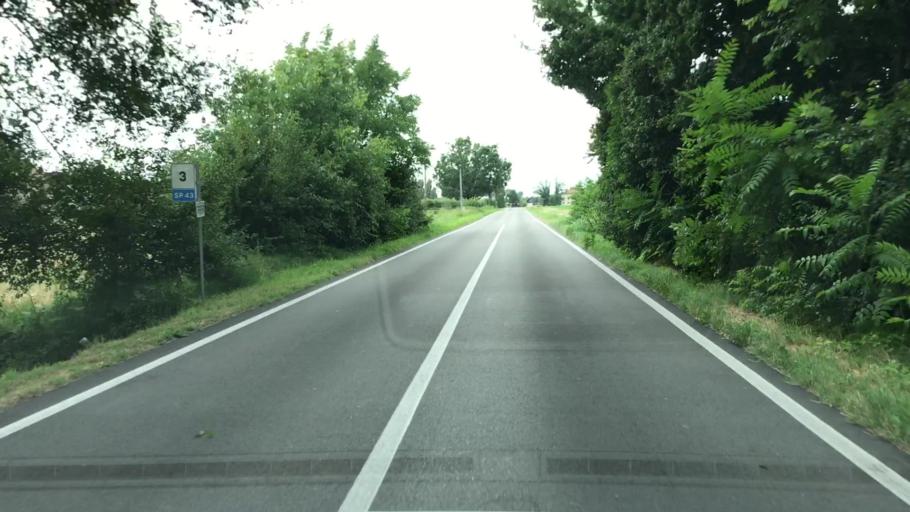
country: IT
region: Lombardy
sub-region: Provincia di Mantova
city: Quistello
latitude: 45.0306
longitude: 10.9975
